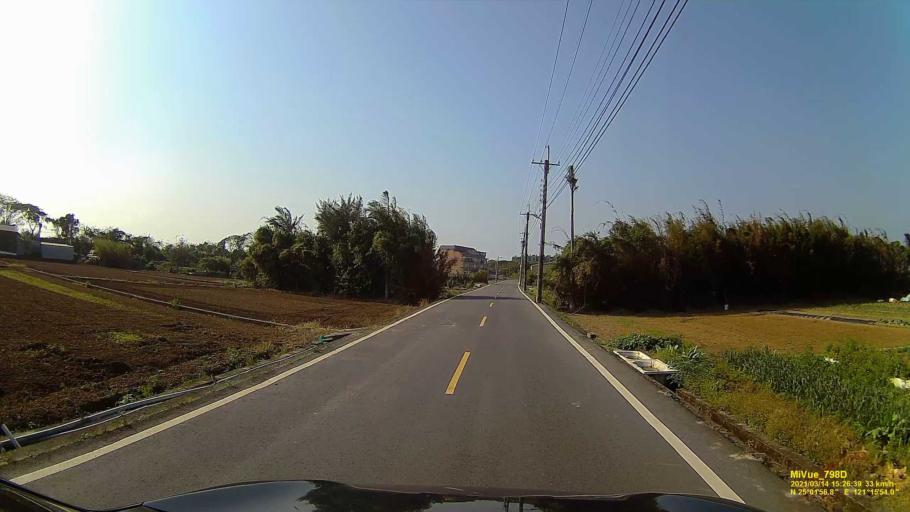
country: TW
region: Taiwan
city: Taoyuan City
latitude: 25.0326
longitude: 121.2649
